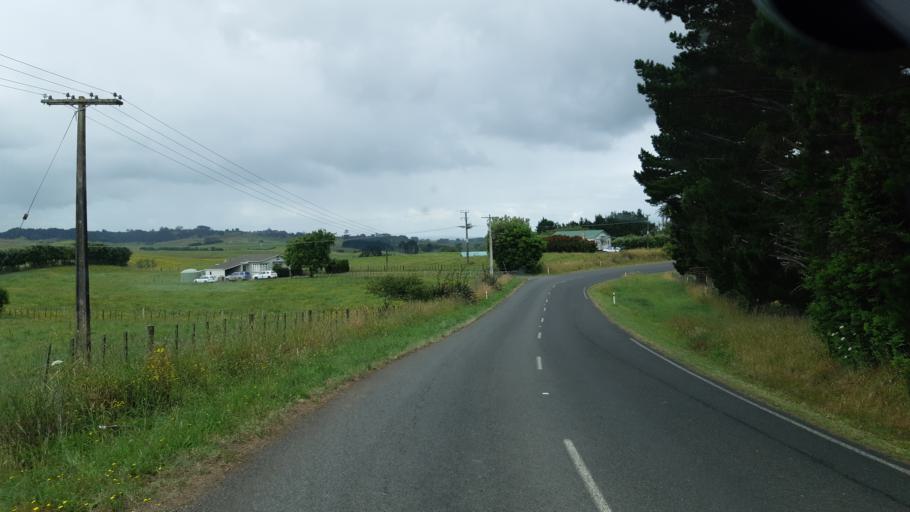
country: NZ
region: Waikato
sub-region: Waikato District
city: Ngaruawahia
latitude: -37.5554
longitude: 175.0690
